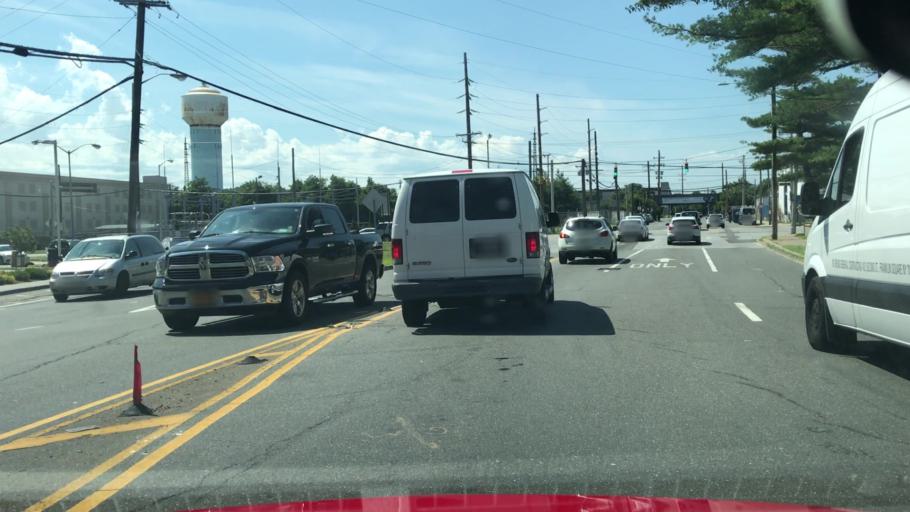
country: US
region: New York
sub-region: Nassau County
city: Lynbrook
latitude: 40.6599
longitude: -73.6572
